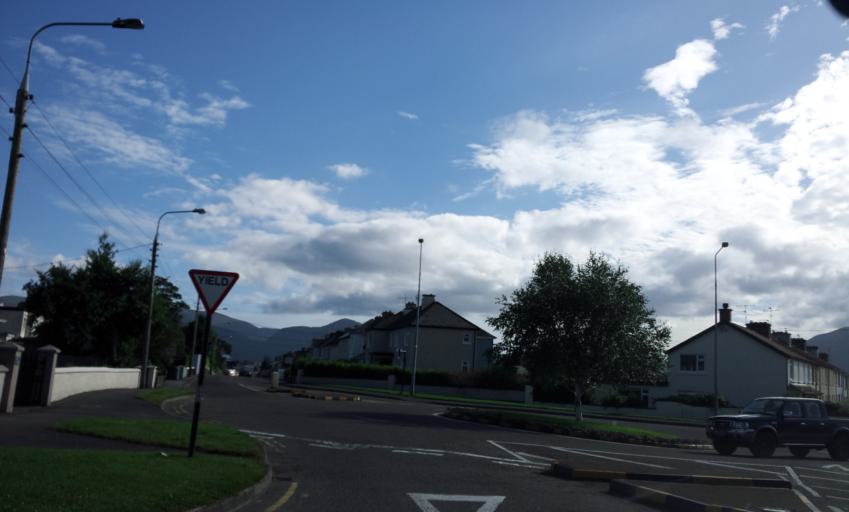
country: IE
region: Munster
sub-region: Ciarrai
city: Cill Airne
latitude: 52.0642
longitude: -9.5061
